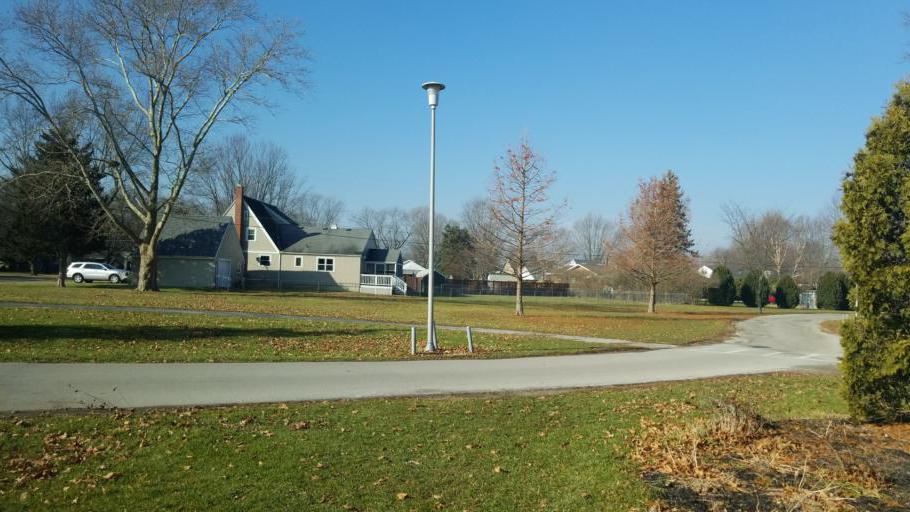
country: US
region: Ohio
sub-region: Seneca County
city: Tiffin
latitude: 41.1028
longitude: -83.1594
